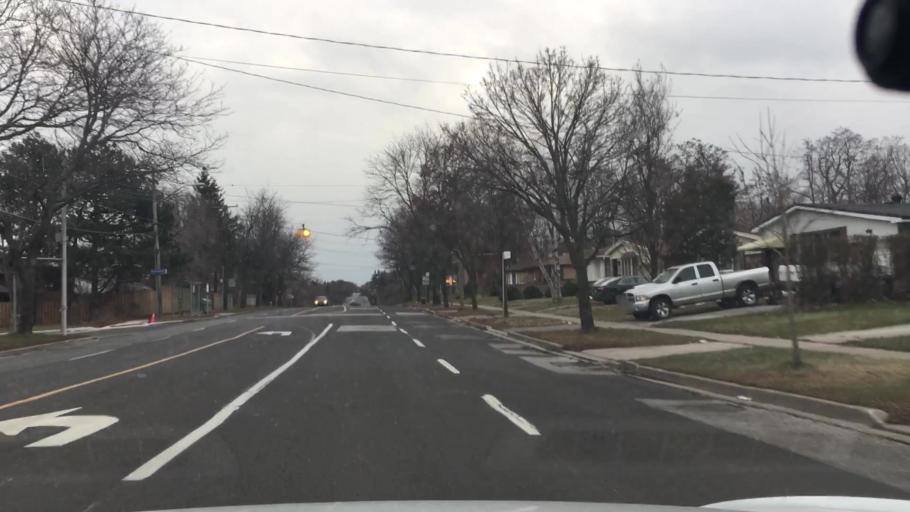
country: CA
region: Ontario
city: Scarborough
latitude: 43.7559
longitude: -79.2351
